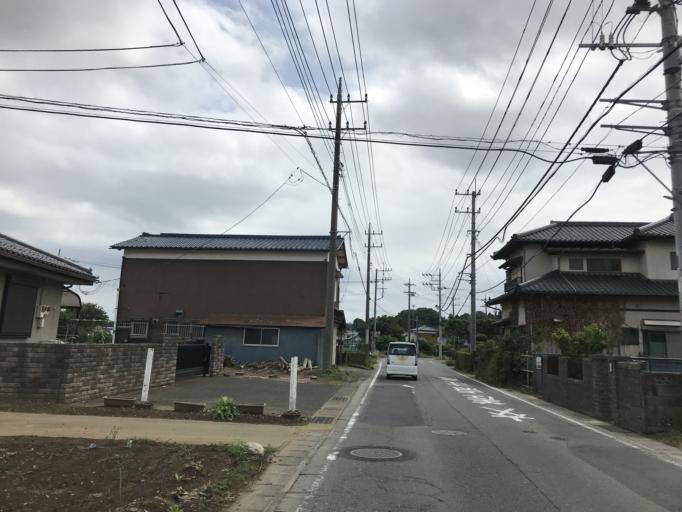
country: JP
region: Ibaraki
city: Ushiku
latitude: 35.9782
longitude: 140.0976
